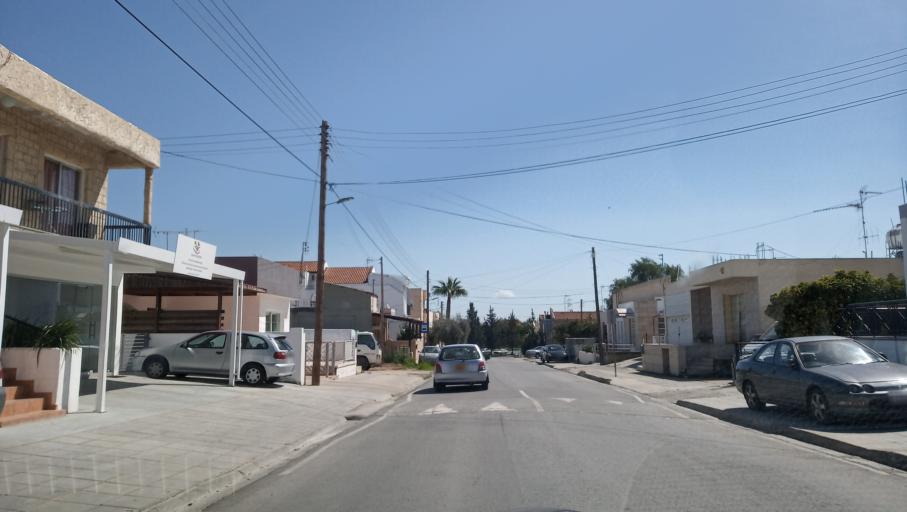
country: CY
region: Lefkosia
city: Kato Deftera
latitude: 35.1222
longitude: 33.2986
